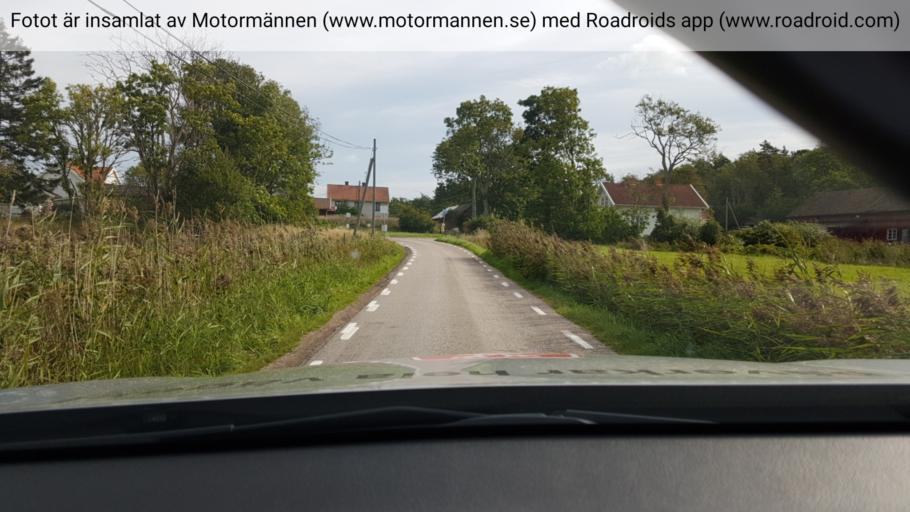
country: SE
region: Vaestra Goetaland
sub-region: Lysekils Kommun
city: Lysekil
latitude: 58.2308
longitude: 11.5349
